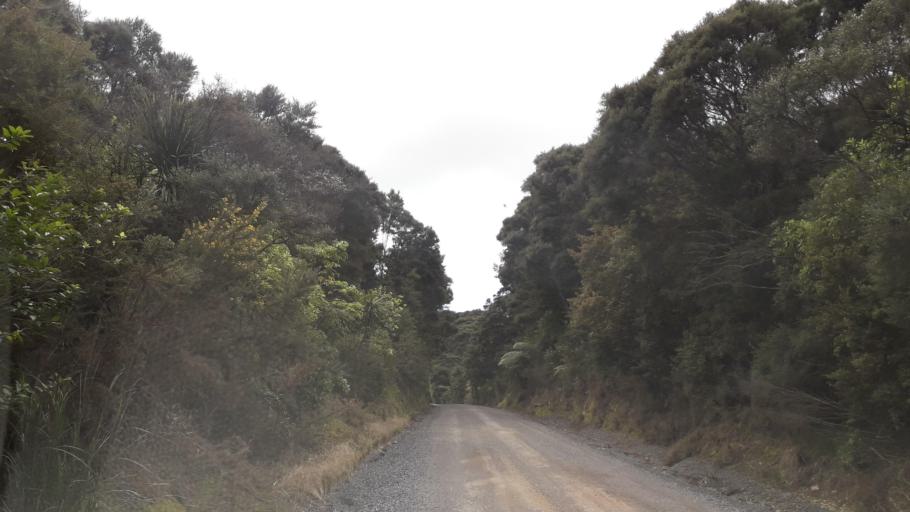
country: NZ
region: Northland
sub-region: Far North District
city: Paihia
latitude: -35.3133
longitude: 174.2241
